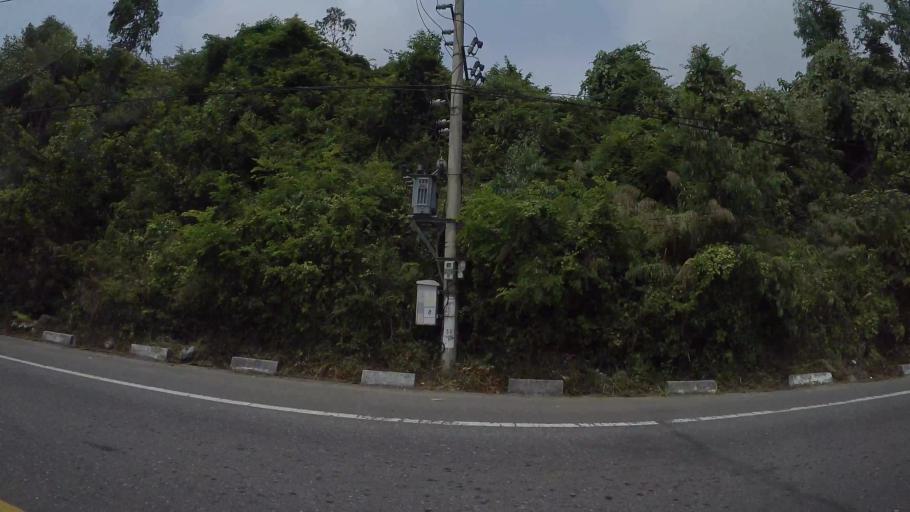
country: VN
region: Da Nang
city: Son Tra
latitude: 16.0987
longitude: 108.2778
